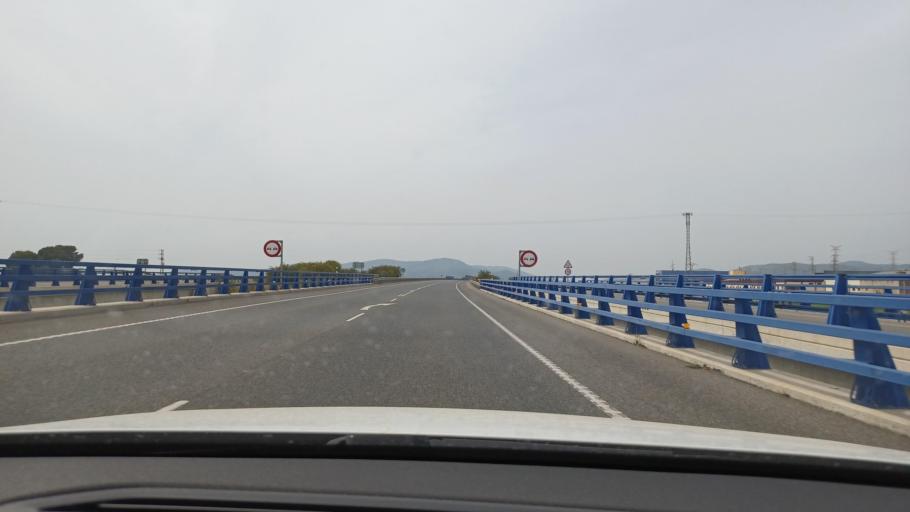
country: ES
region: Valencia
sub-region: Provincia de Castello
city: Benicarlo
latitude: 40.4360
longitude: 0.4088
